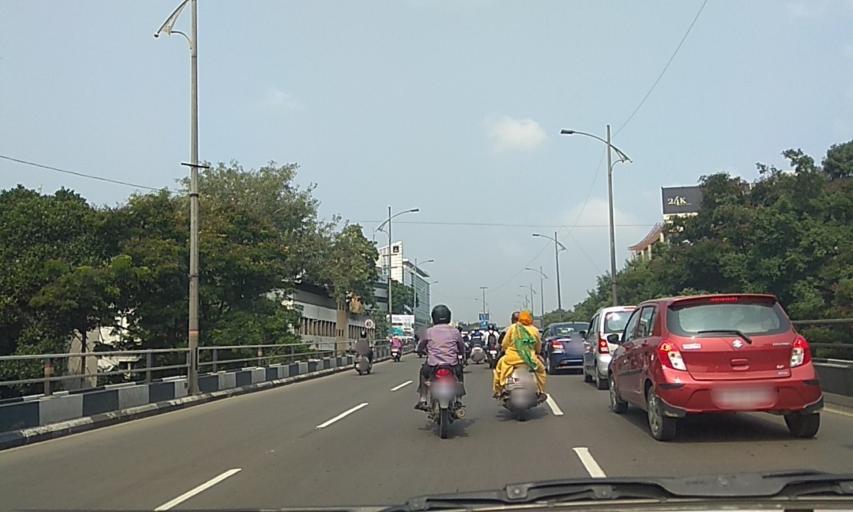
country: IN
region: Maharashtra
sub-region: Pune Division
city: Shivaji Nagar
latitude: 18.5403
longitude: 73.8315
